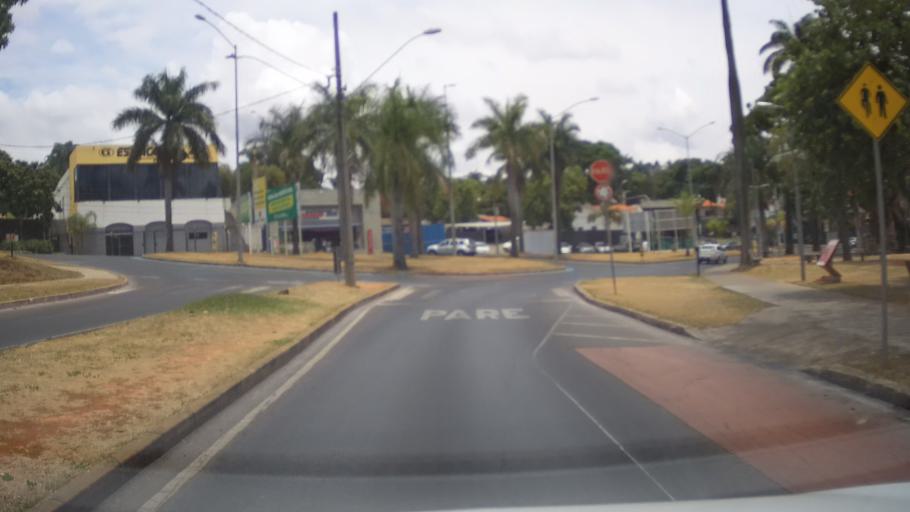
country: BR
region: Minas Gerais
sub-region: Belo Horizonte
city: Belo Horizonte
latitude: -19.8539
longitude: -43.9684
